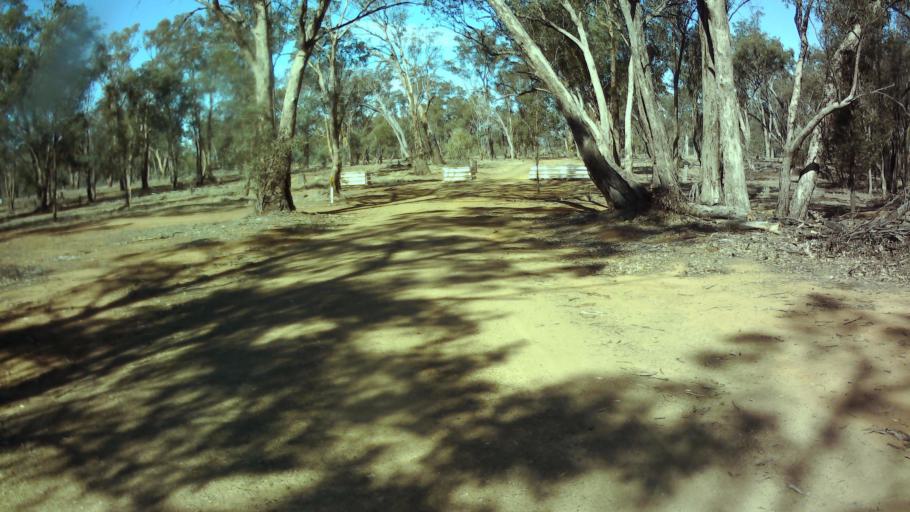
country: AU
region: New South Wales
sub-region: Weddin
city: Grenfell
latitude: -33.7338
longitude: 148.0891
